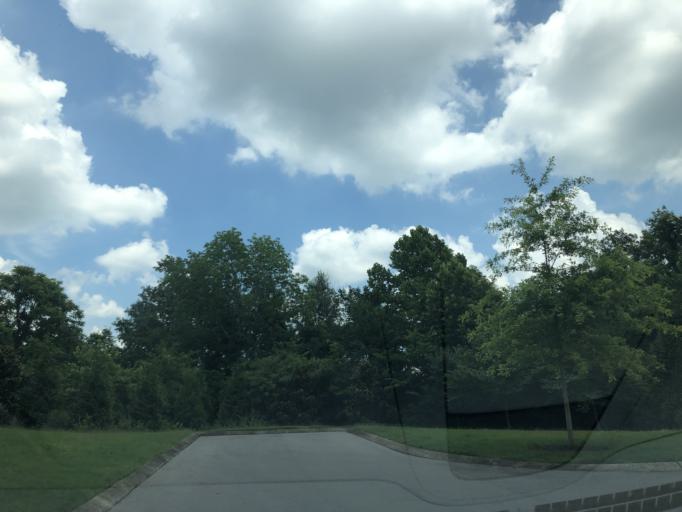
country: US
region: Tennessee
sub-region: Williamson County
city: Nolensville
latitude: 36.0123
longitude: -86.6990
